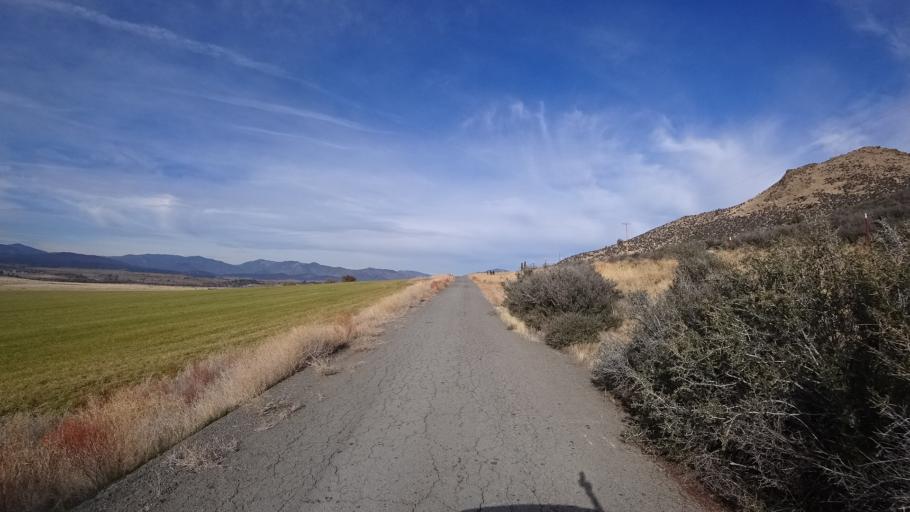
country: US
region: California
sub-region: Siskiyou County
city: Montague
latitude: 41.7077
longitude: -122.5162
